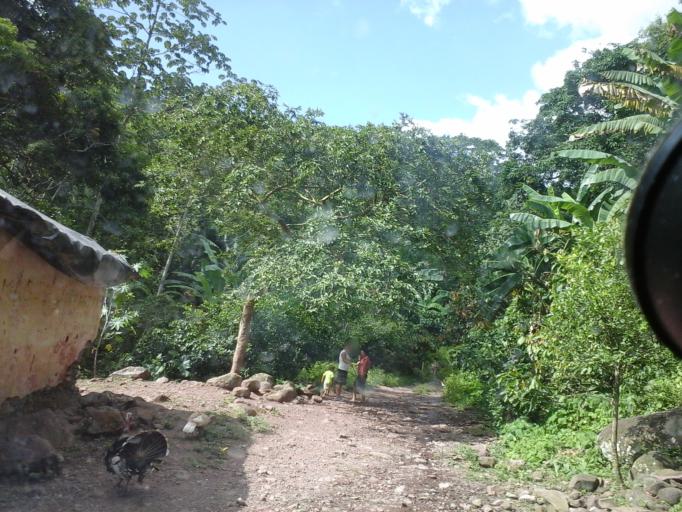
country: CO
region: Cesar
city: Manaure Balcon del Cesar
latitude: 10.2945
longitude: -73.0749
